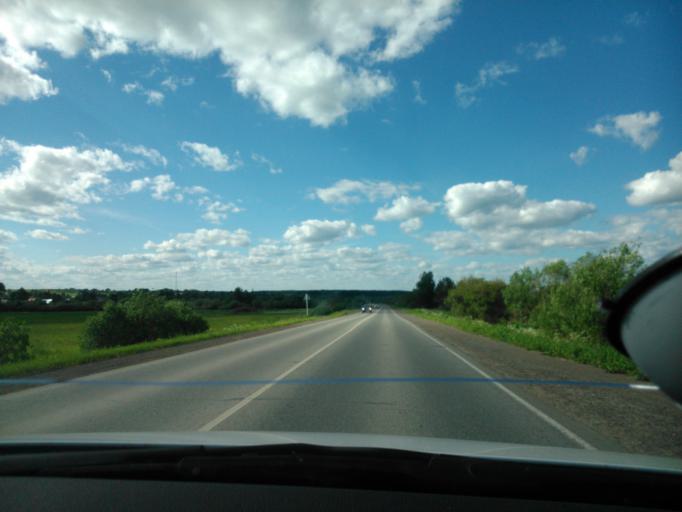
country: RU
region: Perm
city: Ust'-Kachka
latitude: 57.9348
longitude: 55.7594
